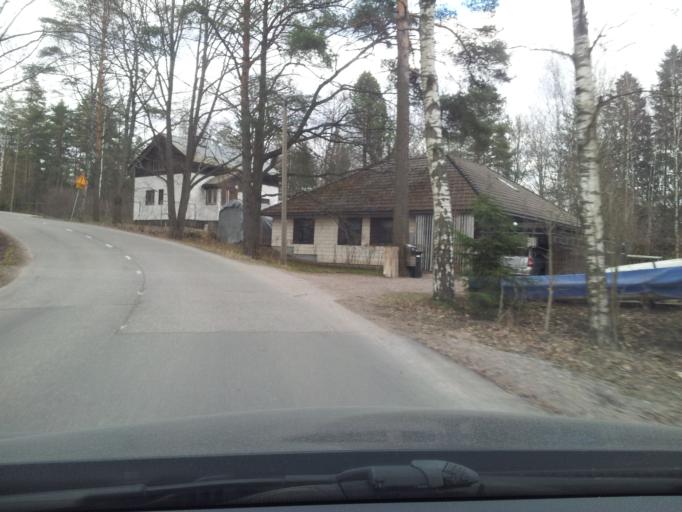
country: FI
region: Uusimaa
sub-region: Helsinki
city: Kilo
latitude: 60.2101
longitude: 24.8013
